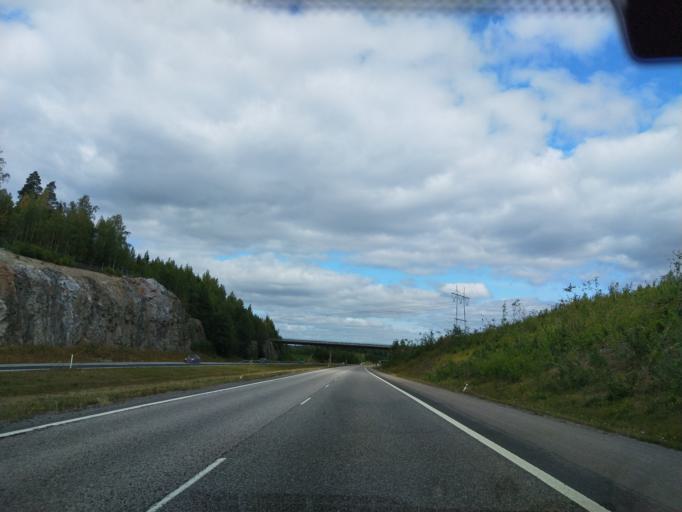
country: FI
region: Uusimaa
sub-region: Helsinki
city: Nurmijaervi
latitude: 60.3873
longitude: 24.8149
